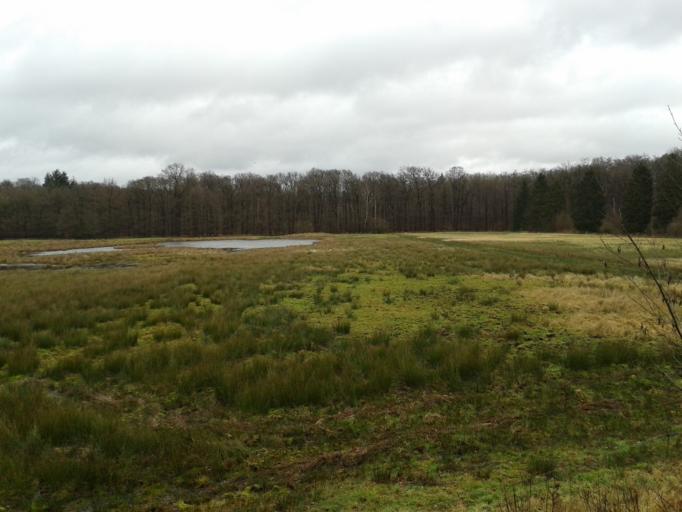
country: DE
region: Lower Saxony
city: Bergen an der Dumme
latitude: 52.9092
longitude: 10.9739
